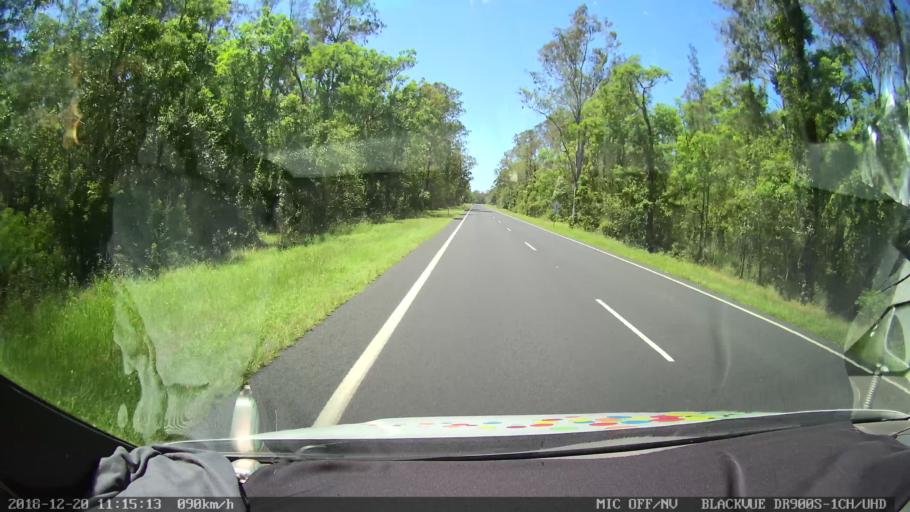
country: AU
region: New South Wales
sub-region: Richmond Valley
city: Casino
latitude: -29.0105
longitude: 153.0073
